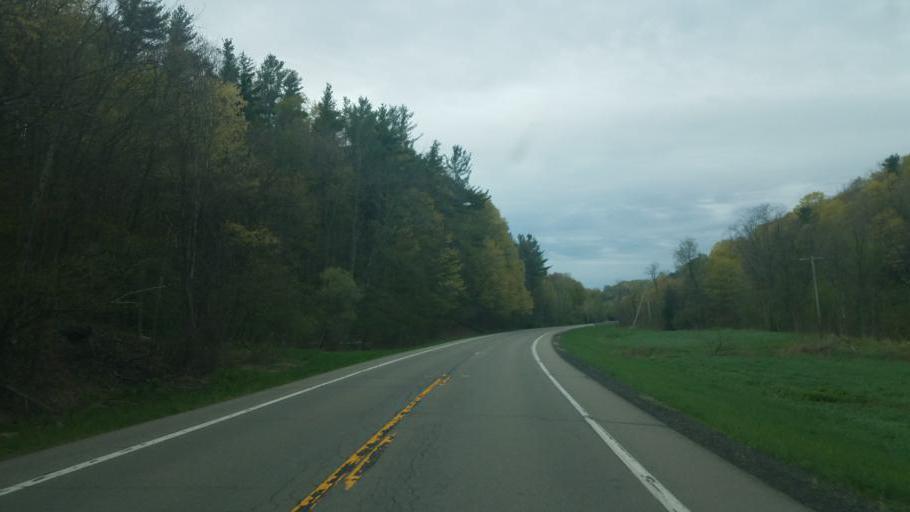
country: US
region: New York
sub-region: Steuben County
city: Canisteo
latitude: 42.1856
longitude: -77.5376
